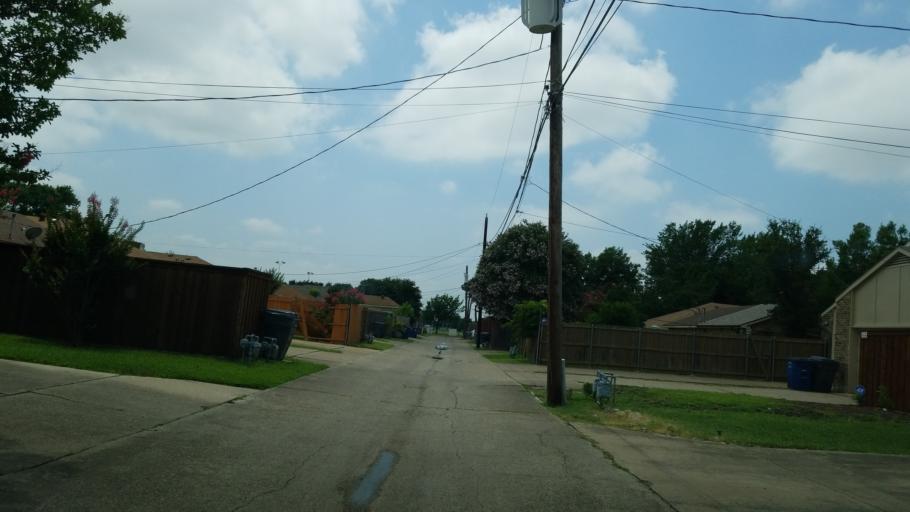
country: US
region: Texas
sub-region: Dallas County
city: Farmers Branch
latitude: 32.9054
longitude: -96.8755
